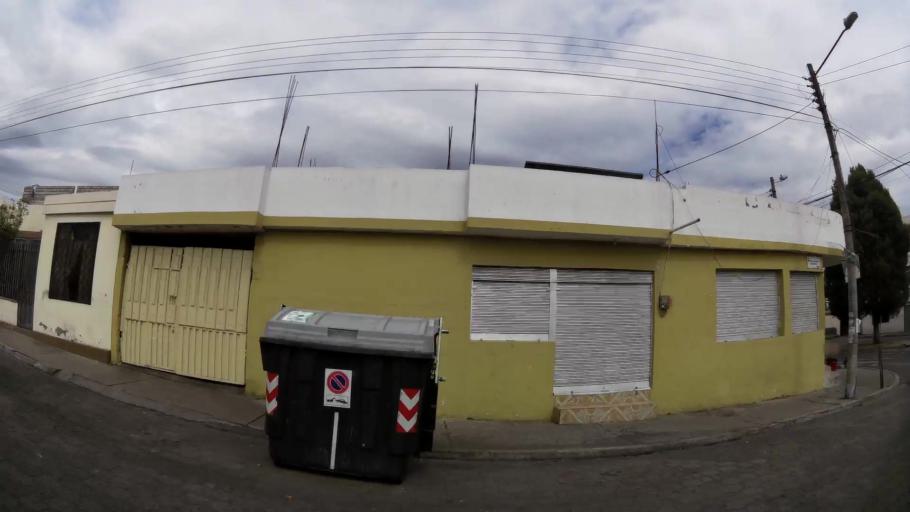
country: EC
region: Cotopaxi
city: Latacunga
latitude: -0.9258
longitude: -78.6236
